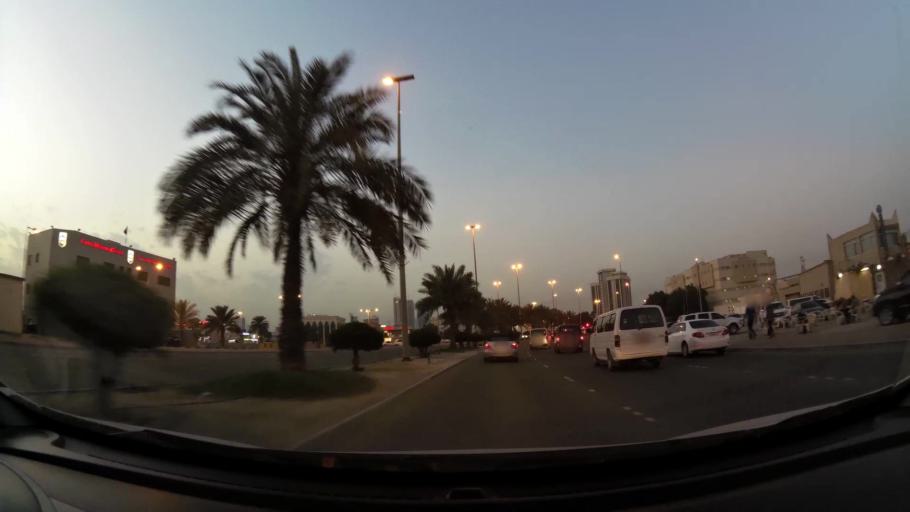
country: BH
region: Manama
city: Jidd Hafs
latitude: 26.2152
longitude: 50.5652
